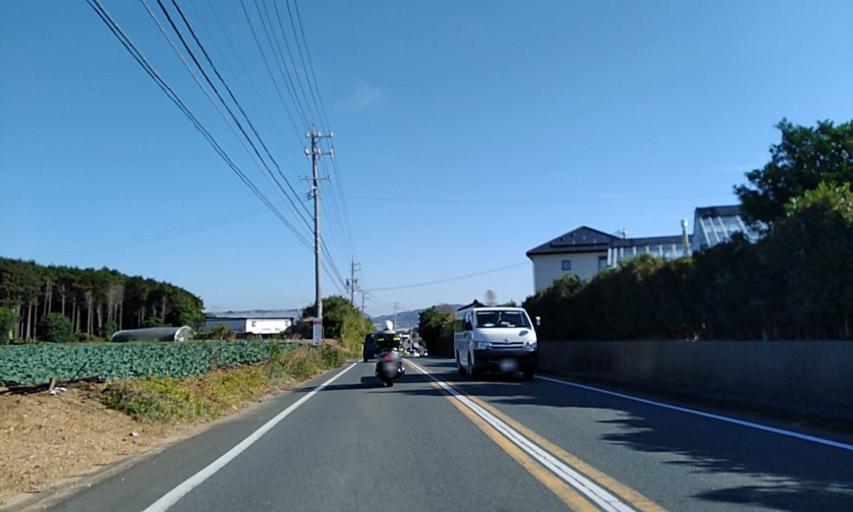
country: JP
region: Aichi
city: Tahara
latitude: 34.6057
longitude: 137.1769
